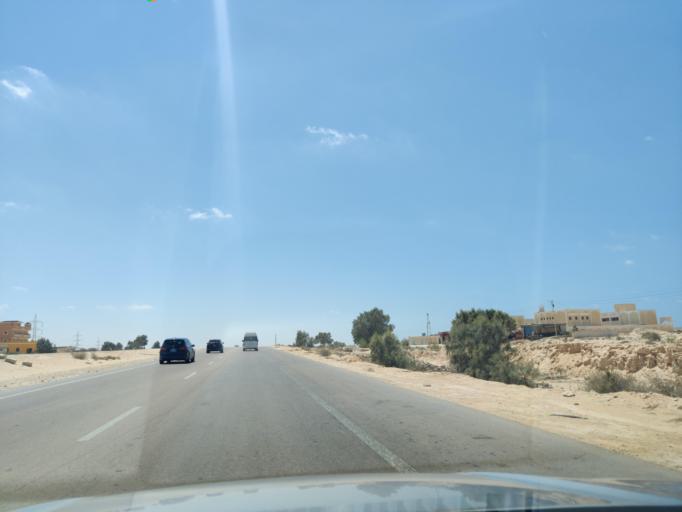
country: EG
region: Muhafazat Matruh
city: Al `Alamayn
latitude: 31.0701
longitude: 28.1506
